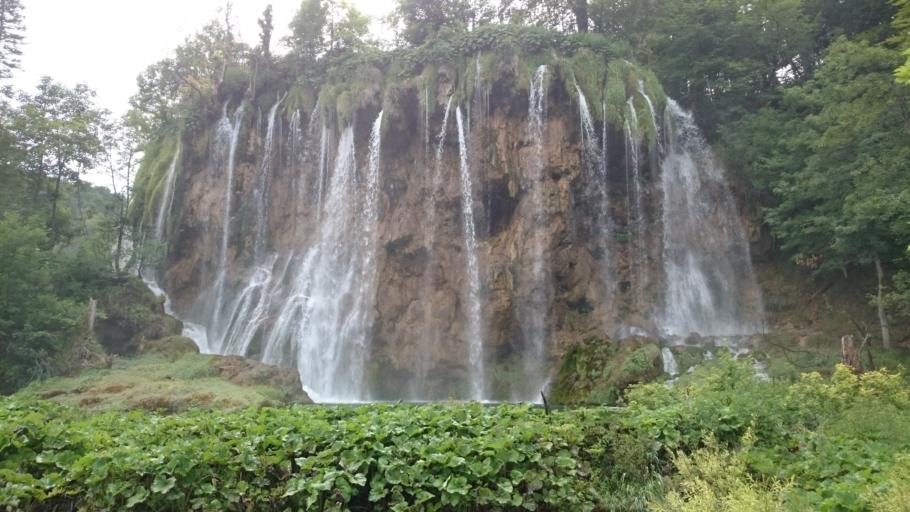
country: HR
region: Licko-Senjska
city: Jezerce
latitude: 44.8782
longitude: 15.6085
